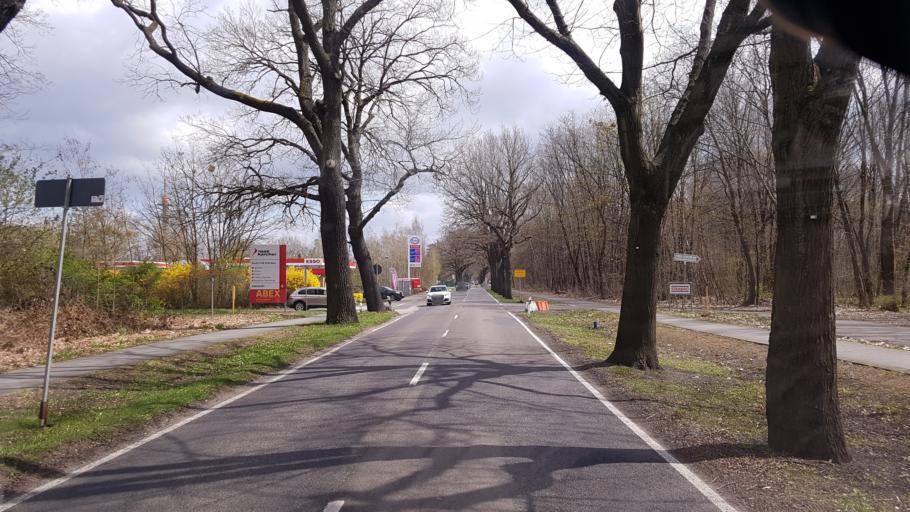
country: DE
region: Brandenburg
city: Senftenberg
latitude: 51.5257
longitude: 13.9711
